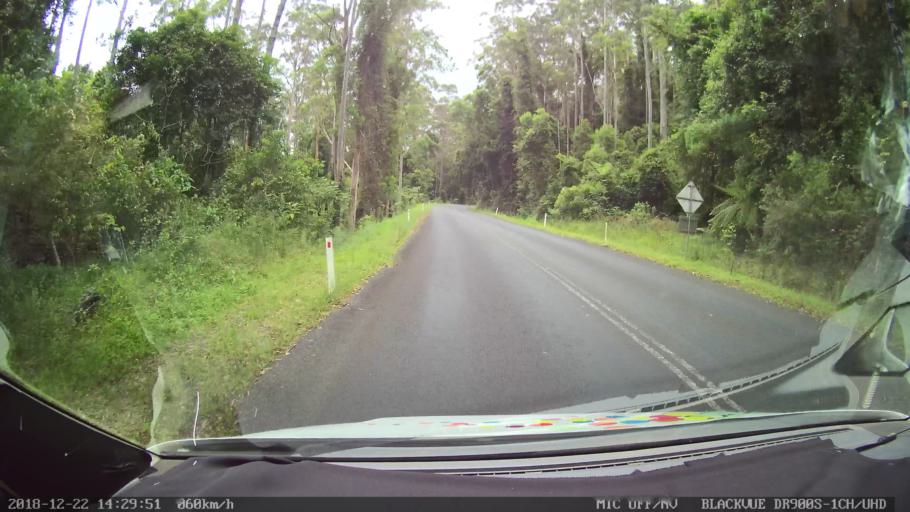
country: AU
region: New South Wales
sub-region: Bellingen
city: Dorrigo
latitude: -30.0805
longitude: 152.6343
